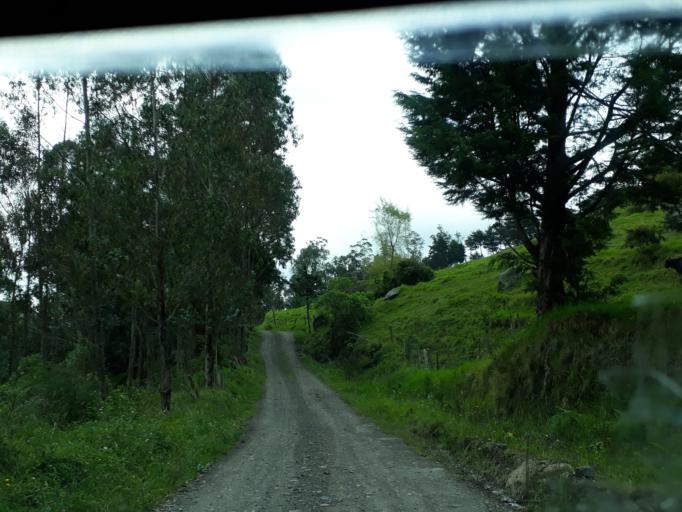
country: CO
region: Cundinamarca
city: Carmen de Carupa
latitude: 5.3778
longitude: -73.9814
